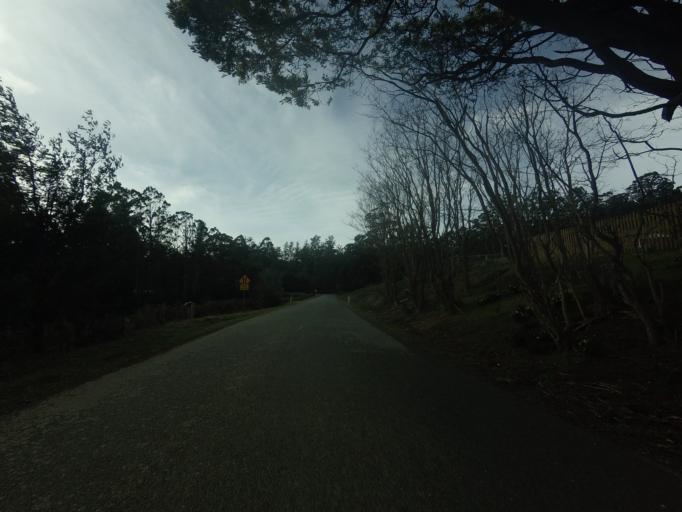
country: AU
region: Tasmania
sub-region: Huon Valley
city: Huonville
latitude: -43.0501
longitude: 147.1091
